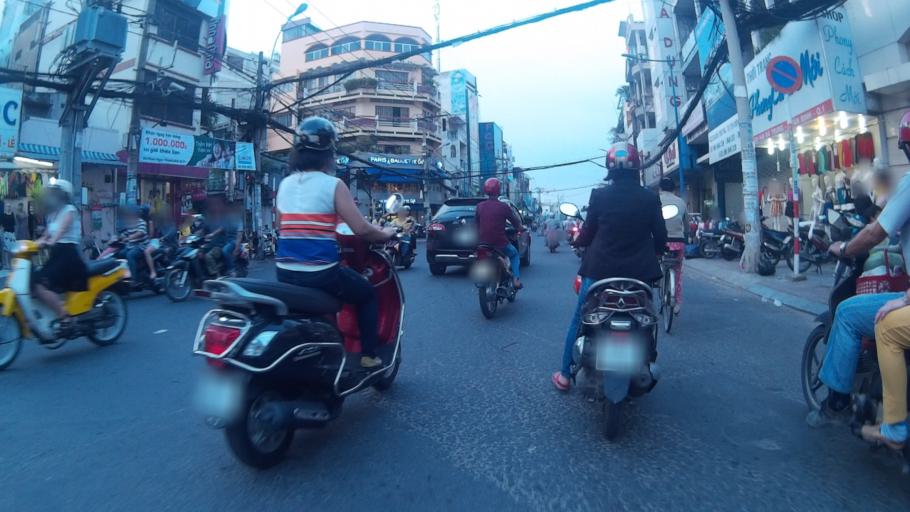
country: VN
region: Ho Chi Minh City
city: Quan Phu Nhuan
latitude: 10.7913
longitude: 106.6876
